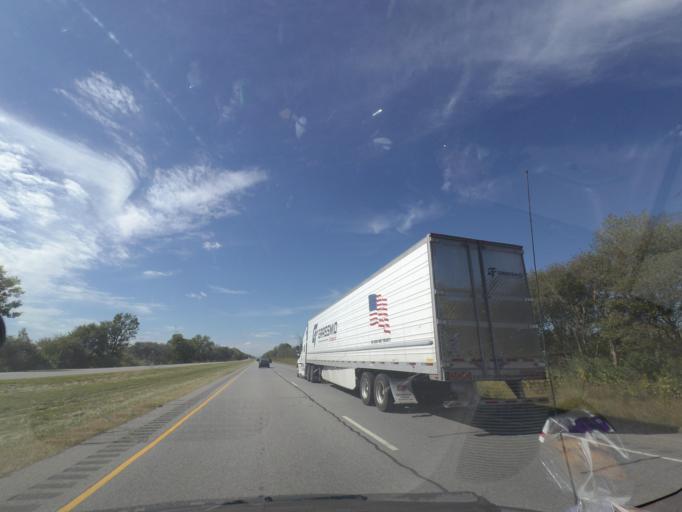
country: US
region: Indiana
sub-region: Boone County
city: Thorntown
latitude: 39.9870
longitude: -86.6968
